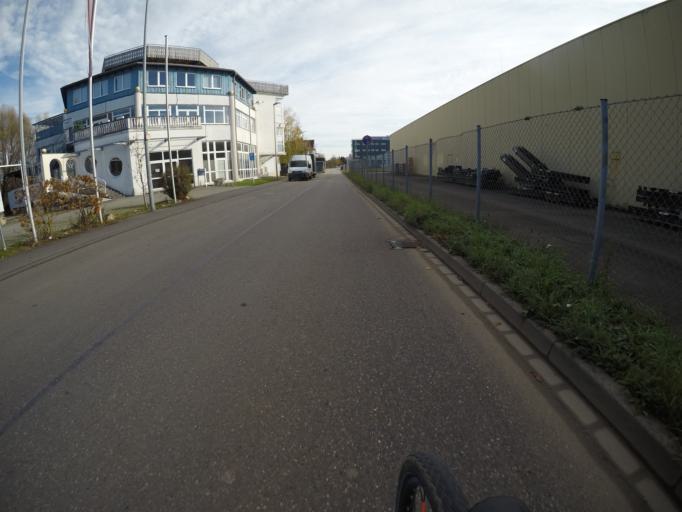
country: DE
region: Baden-Wuerttemberg
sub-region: Regierungsbezirk Stuttgart
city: Schorndorf
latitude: 48.8115
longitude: 9.5359
